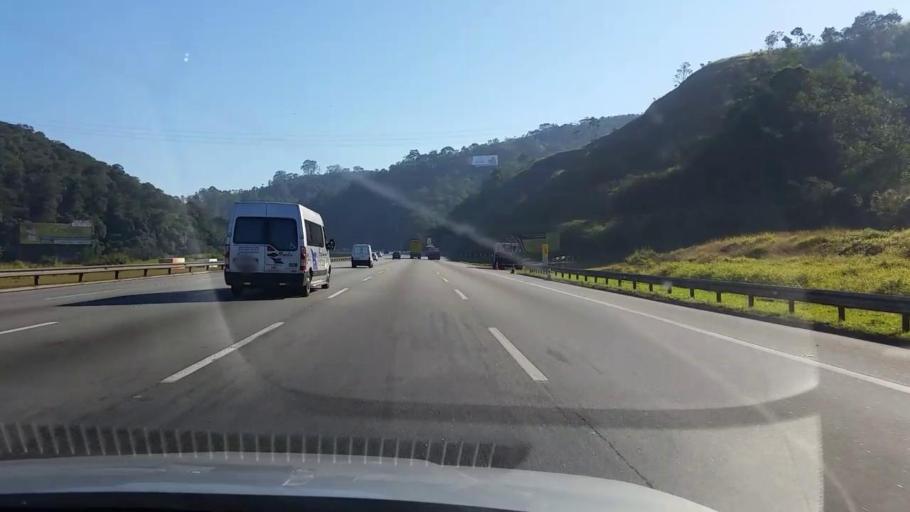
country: BR
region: Sao Paulo
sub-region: Cajamar
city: Cajamar
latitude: -23.2993
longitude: -46.8408
